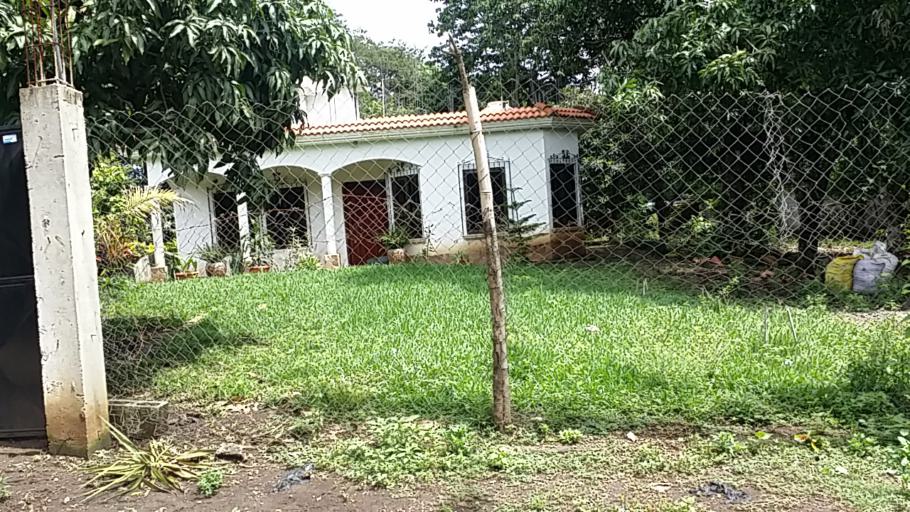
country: GT
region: Santa Rosa
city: Pueblo Nuevo Vinas
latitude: 14.3298
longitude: -90.5154
